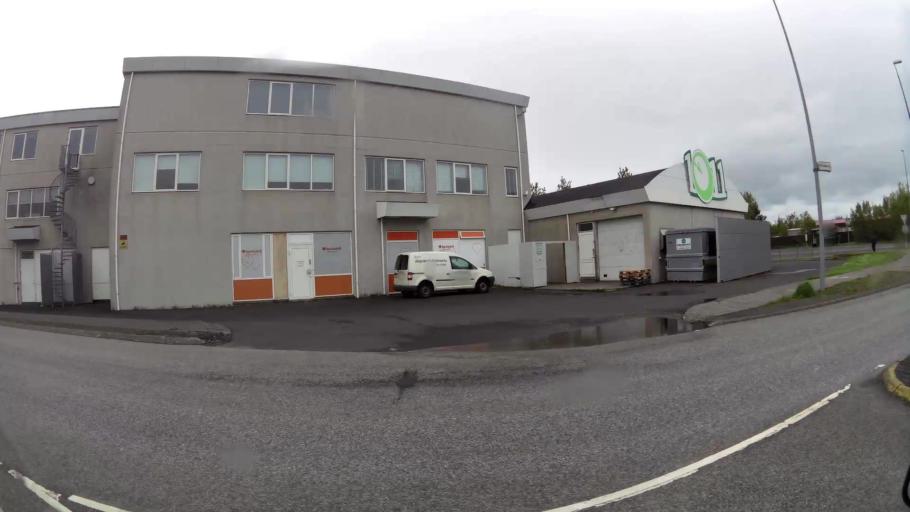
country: IS
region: Capital Region
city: Hafnarfjoerdur
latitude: 64.0667
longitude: -21.9356
